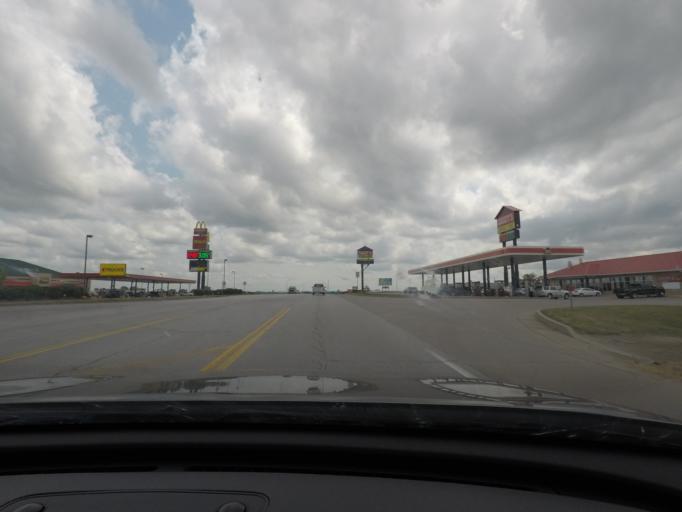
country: US
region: Missouri
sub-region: Lafayette County
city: Higginsville
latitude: 39.0043
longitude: -93.7353
